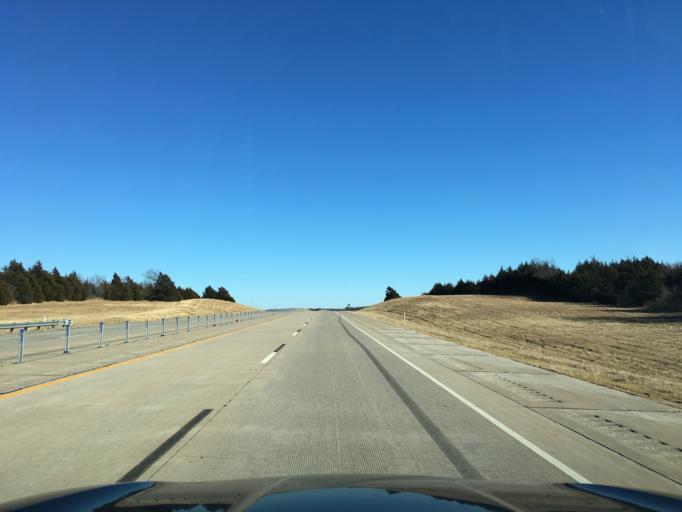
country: US
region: Oklahoma
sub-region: Payne County
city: Yale
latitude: 36.2251
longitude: -96.6240
